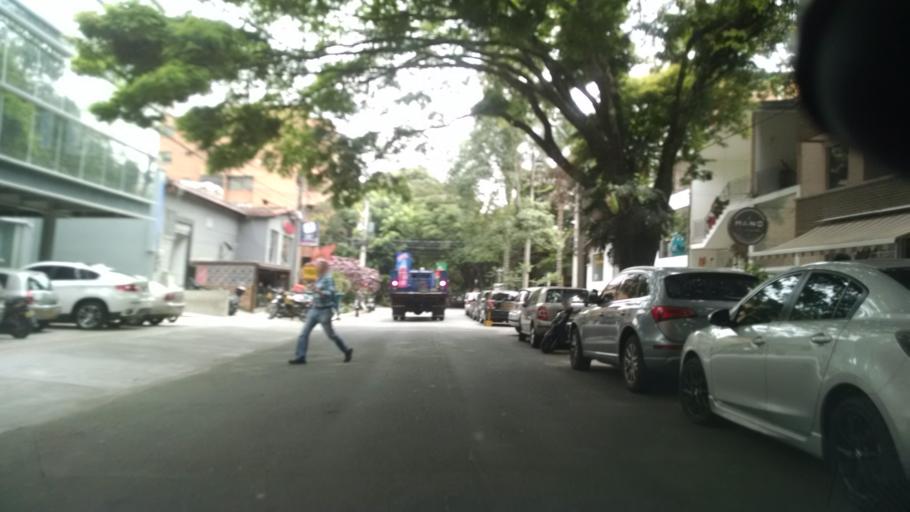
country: CO
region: Antioquia
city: Medellin
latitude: 6.2109
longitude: -75.5652
